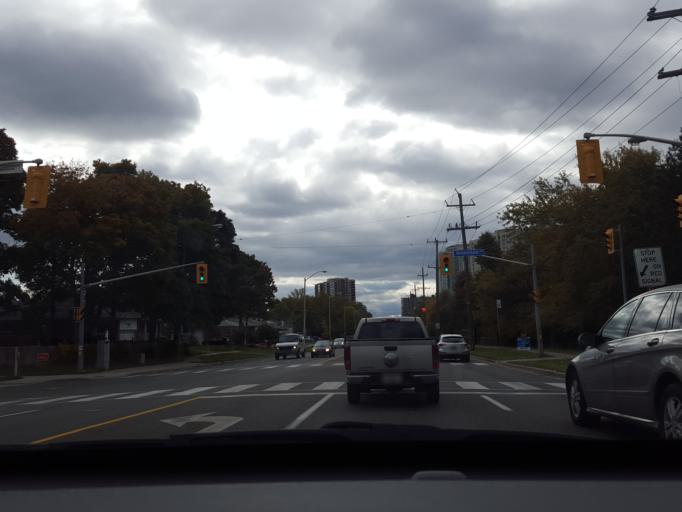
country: CA
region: Ontario
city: Scarborough
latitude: 43.7912
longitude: -79.2920
